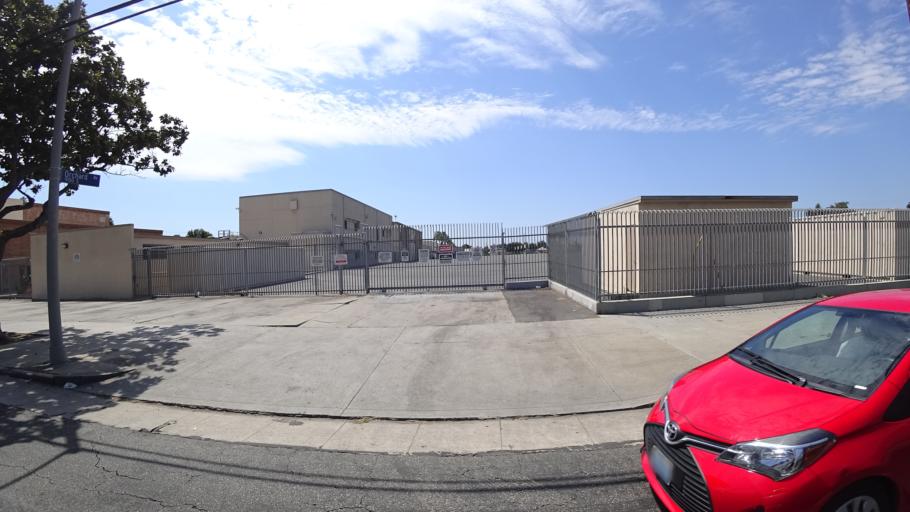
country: US
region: California
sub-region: Los Angeles County
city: Westmont
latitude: 33.9528
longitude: -118.2882
